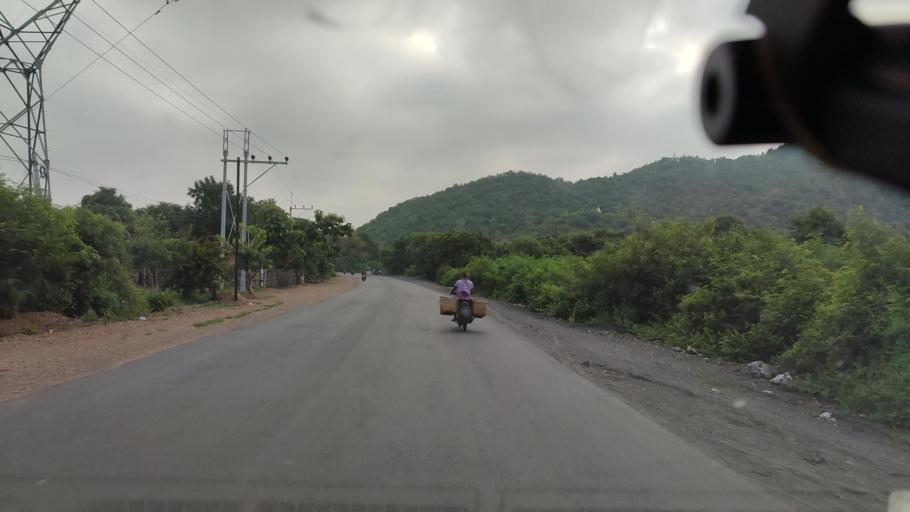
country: MM
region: Mandalay
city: Mandalay
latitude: 22.1120
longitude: 96.1578
